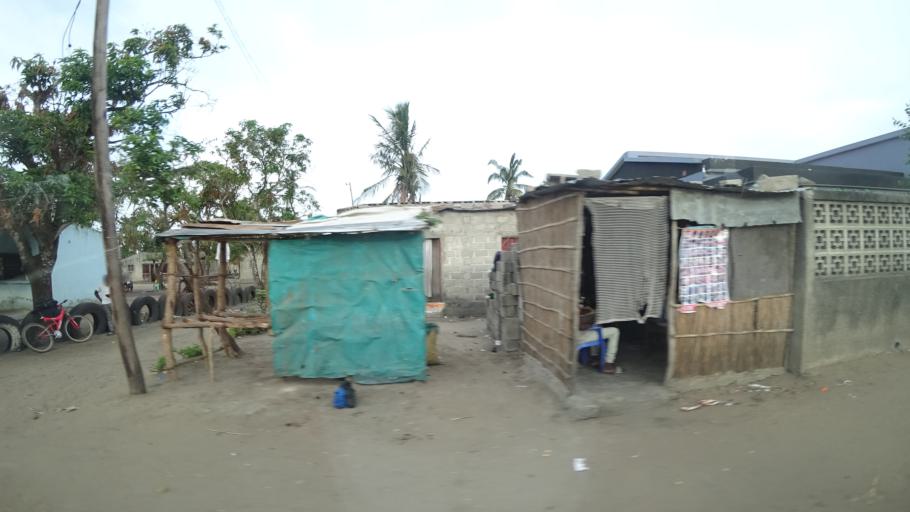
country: MZ
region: Sofala
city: Beira
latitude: -19.7726
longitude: 34.8860
